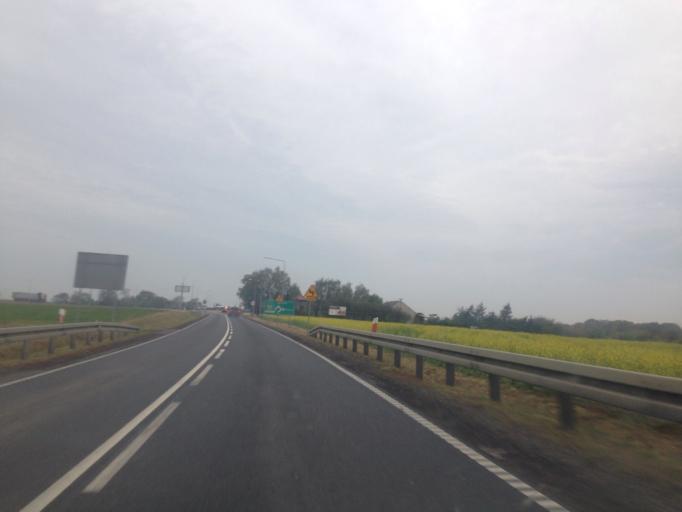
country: PL
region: Kujawsko-Pomorskie
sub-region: Powiat mogilenski
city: Mogilno
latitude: 52.6230
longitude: 18.0138
